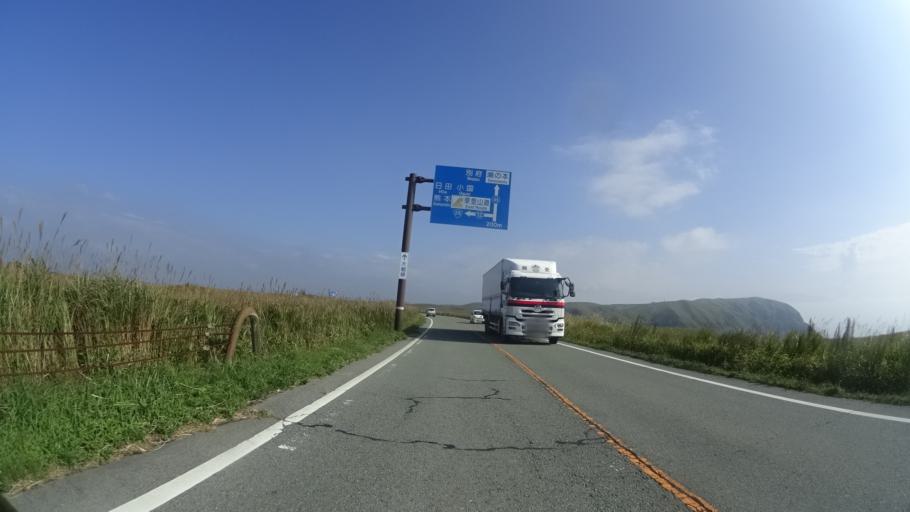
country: JP
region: Kumamoto
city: Aso
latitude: 33.0102
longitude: 131.0603
